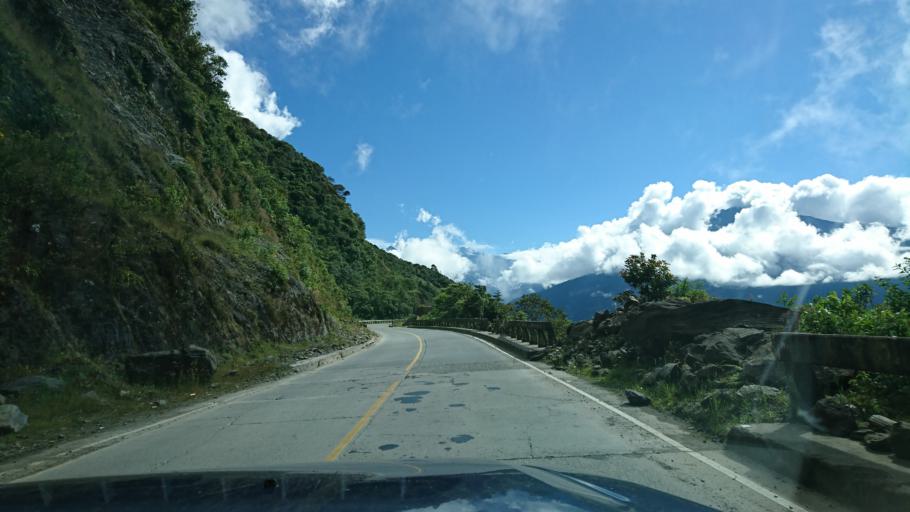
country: BO
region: La Paz
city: Coroico
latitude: -16.2228
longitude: -67.8338
